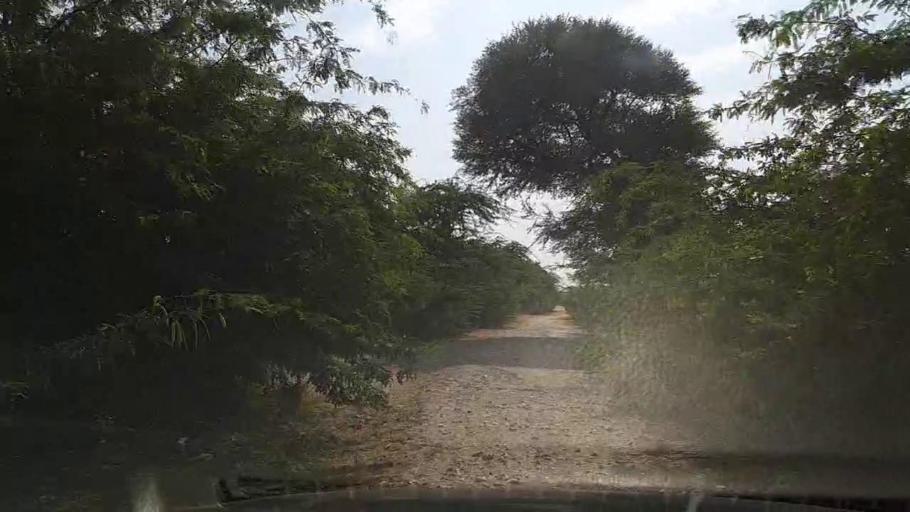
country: PK
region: Sindh
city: Thatta
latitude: 24.7562
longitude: 67.7773
